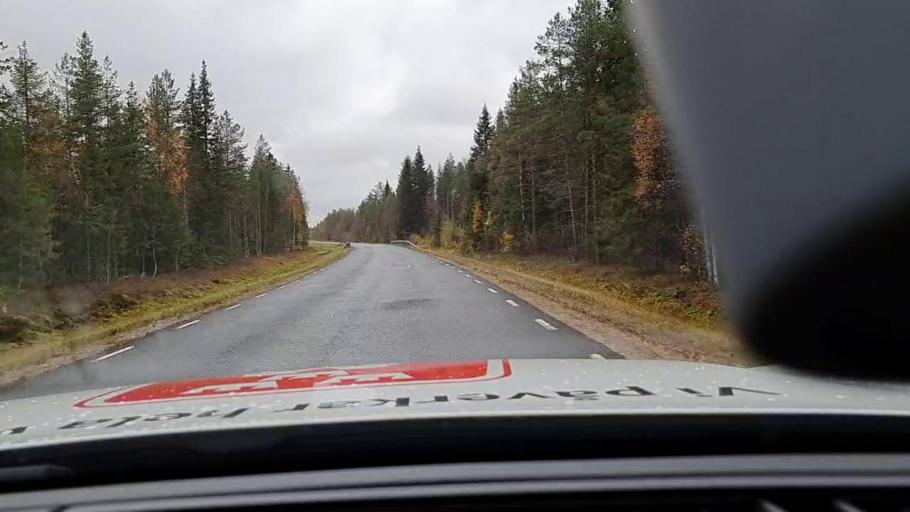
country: SE
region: Norrbotten
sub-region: Haparanda Kommun
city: Haparanda
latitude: 65.9037
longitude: 23.8335
